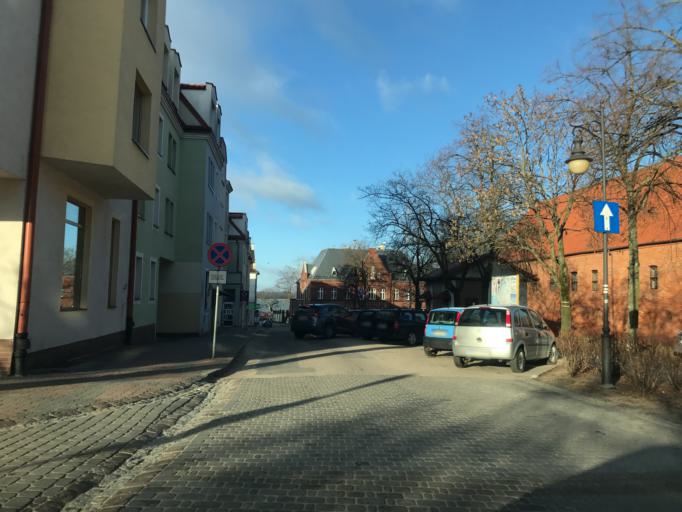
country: PL
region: Warmian-Masurian Voivodeship
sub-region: Powiat ostrodzki
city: Ostroda
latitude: 53.7030
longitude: 19.9622
